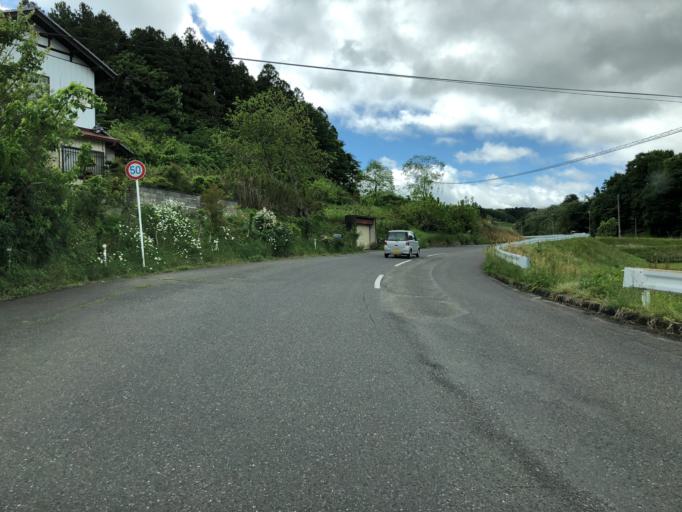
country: JP
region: Fukushima
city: Miharu
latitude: 37.4802
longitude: 140.4691
